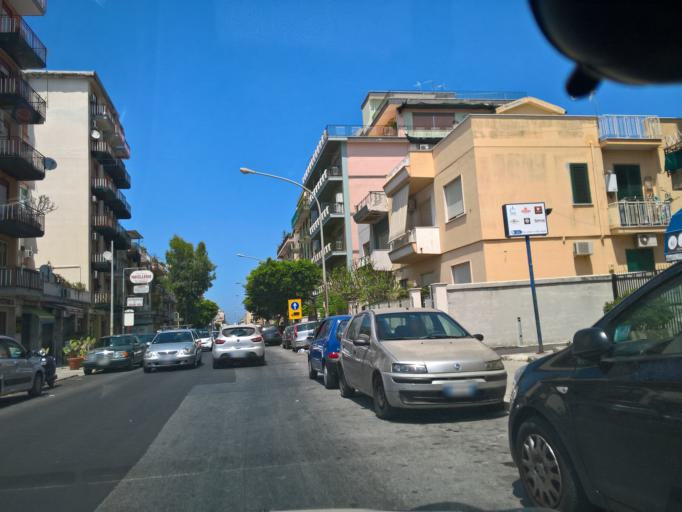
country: IT
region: Sicily
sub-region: Palermo
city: Ciaculli
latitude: 38.0921
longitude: 13.3863
